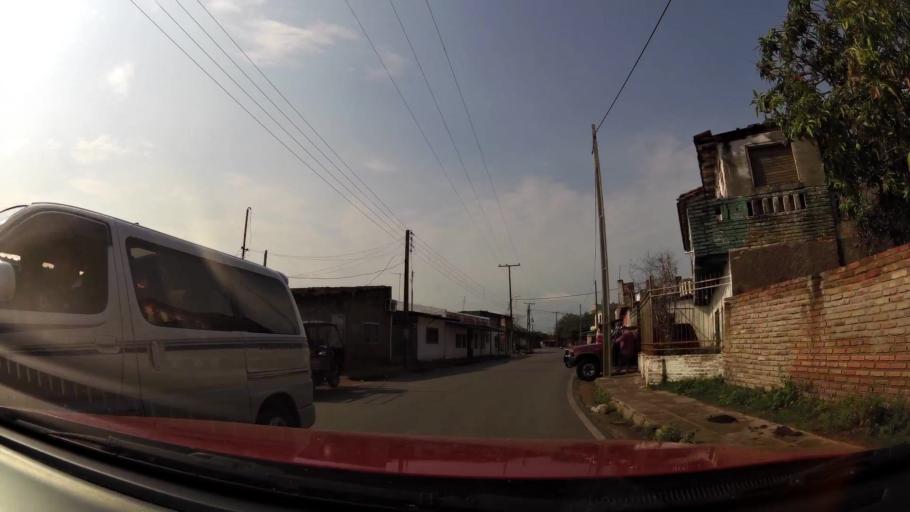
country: PY
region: Asuncion
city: Asuncion
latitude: -25.3099
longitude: -57.6671
